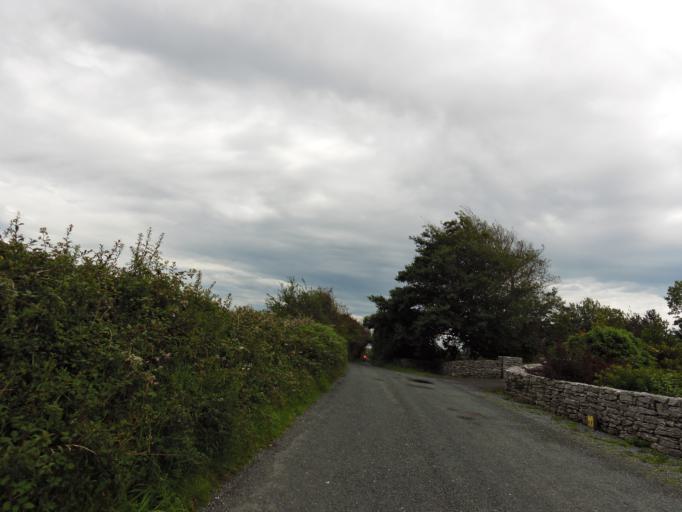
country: IE
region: Connaught
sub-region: County Galway
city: Gaillimh
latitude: 53.3171
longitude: -9.0483
